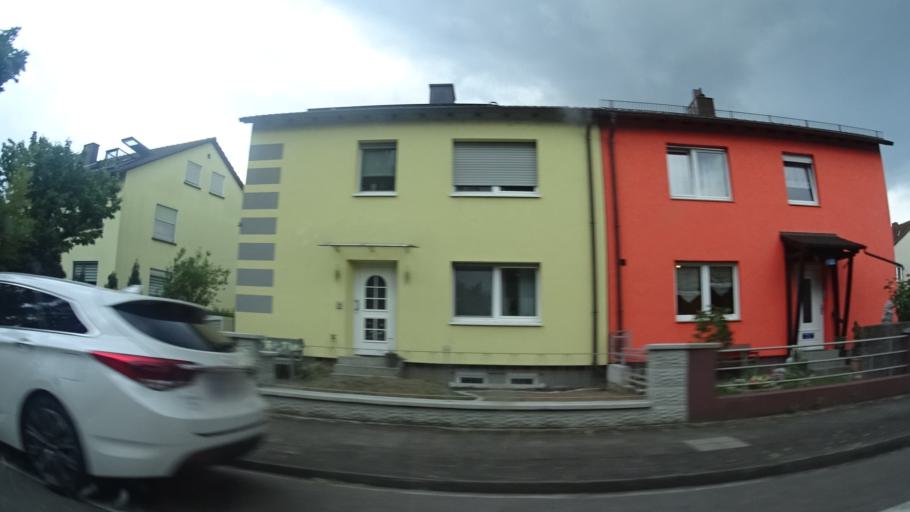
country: DE
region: Rheinland-Pfalz
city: Gartenstadt
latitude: 49.4632
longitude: 8.3999
